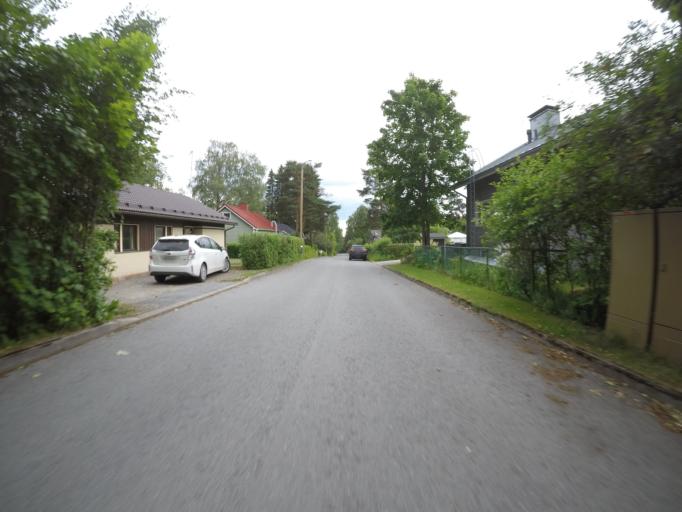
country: FI
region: Haeme
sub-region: Haemeenlinna
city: Haemeenlinna
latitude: 60.9848
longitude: 24.4514
